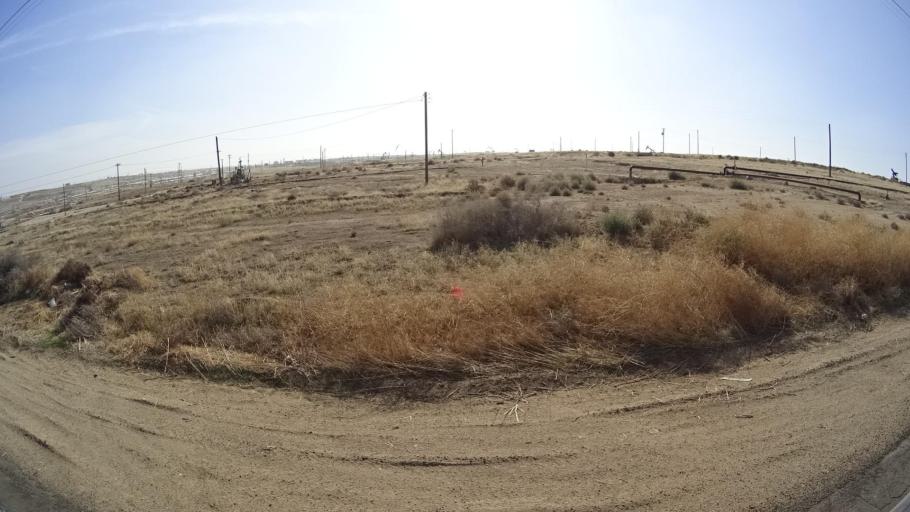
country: US
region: California
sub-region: Kern County
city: Oildale
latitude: 35.5298
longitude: -119.0885
